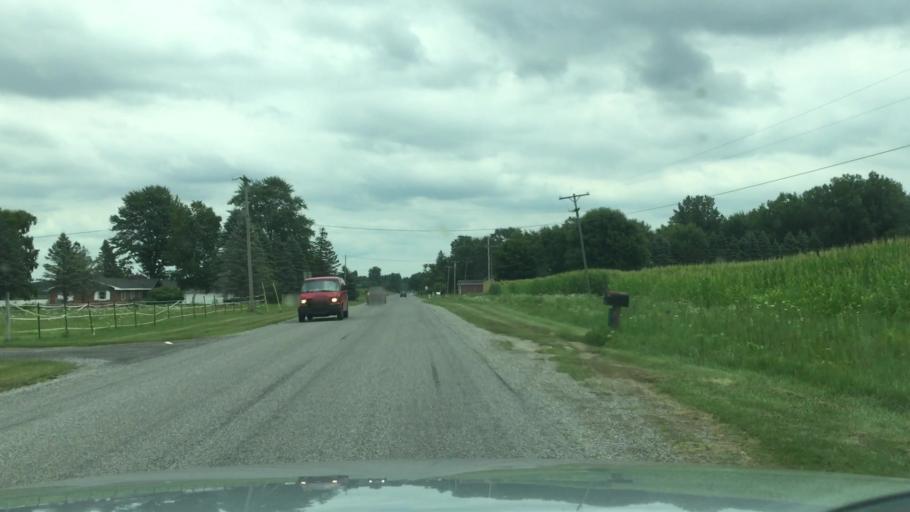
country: US
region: Michigan
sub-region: Saginaw County
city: Bridgeport
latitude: 43.3216
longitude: -83.8377
